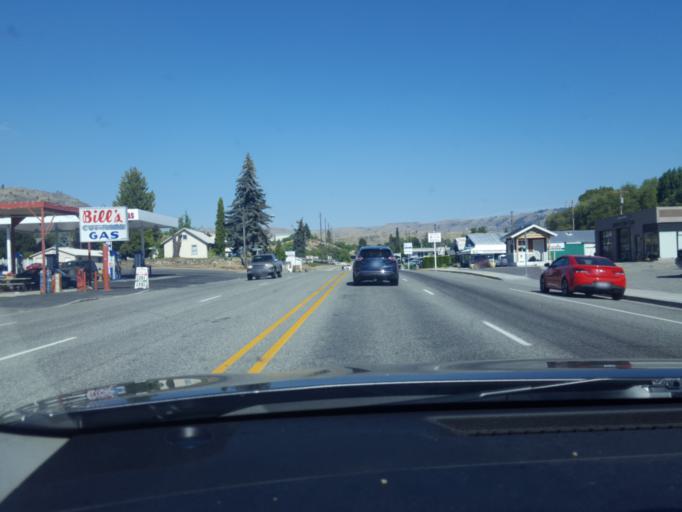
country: US
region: Washington
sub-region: Chelan County
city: Chelan
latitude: 47.8396
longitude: -120.0053
